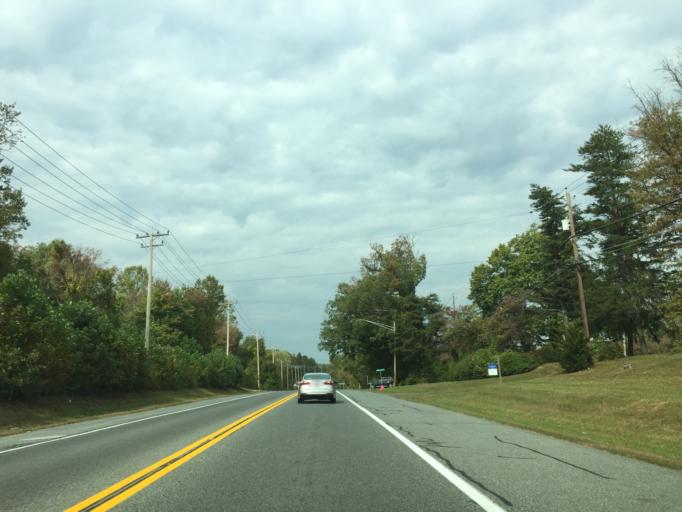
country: US
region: Maryland
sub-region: Harford County
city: Bel Air South
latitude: 39.4876
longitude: -76.3176
